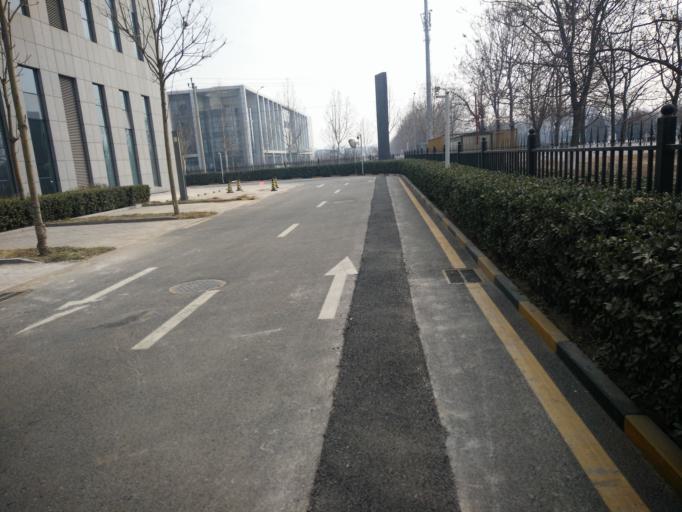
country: CN
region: Beijing
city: Jiugong
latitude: 39.7590
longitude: 116.5104
